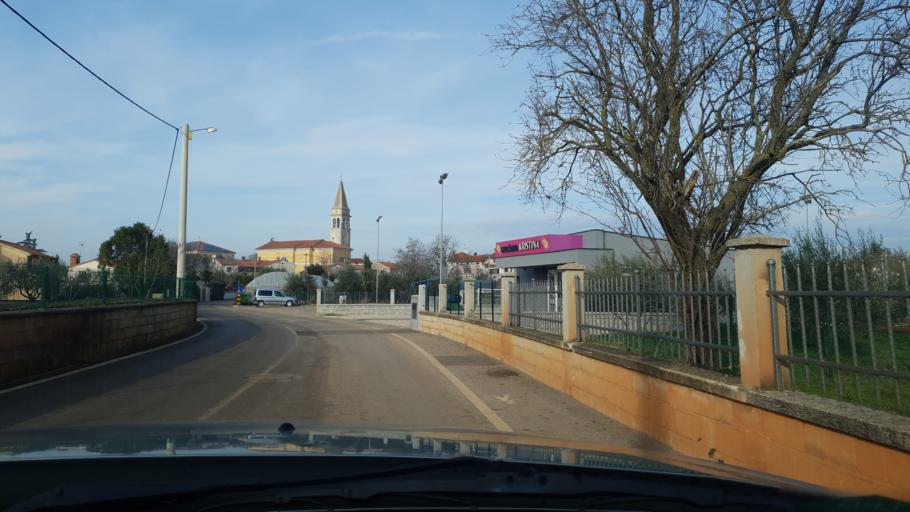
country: HR
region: Istarska
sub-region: Grad Porec
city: Porec
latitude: 45.2614
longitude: 13.6602
